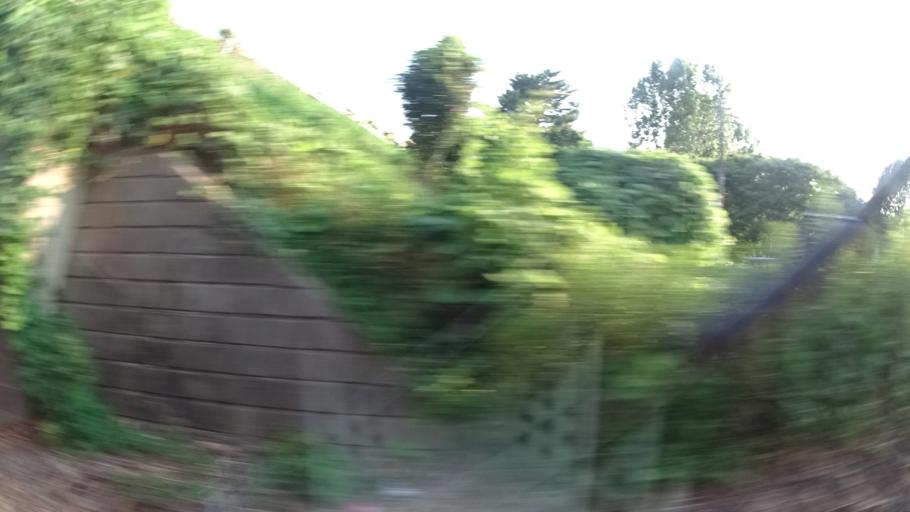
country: JP
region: Ibaraki
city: Mito-shi
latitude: 36.3831
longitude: 140.4415
